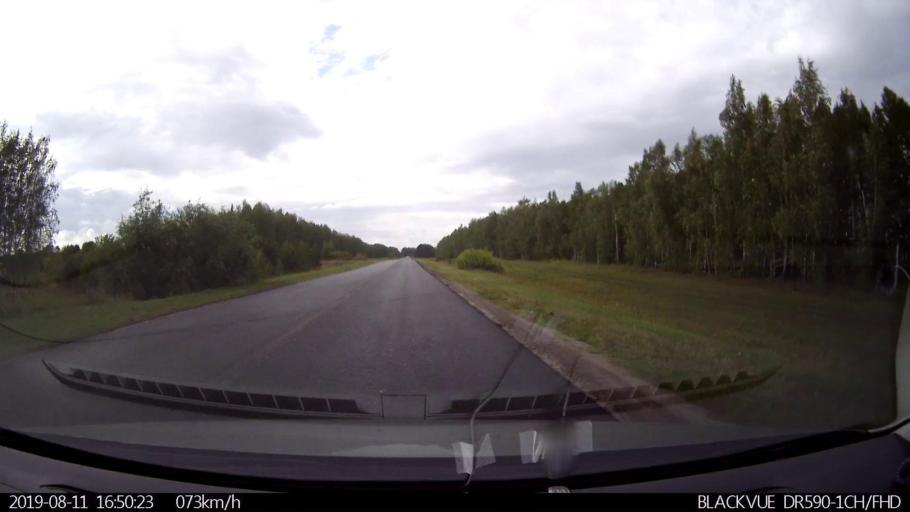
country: RU
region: Ulyanovsk
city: Mayna
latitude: 54.2283
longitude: 47.6880
